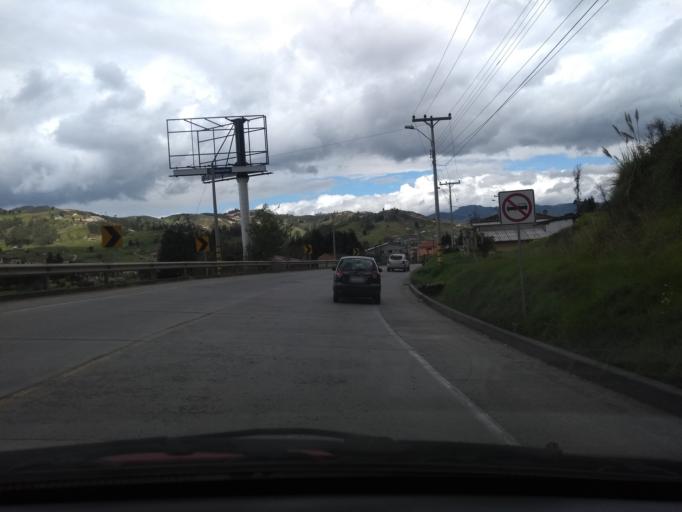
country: EC
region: Azuay
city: Cuenca
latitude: -3.0096
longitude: -79.0396
